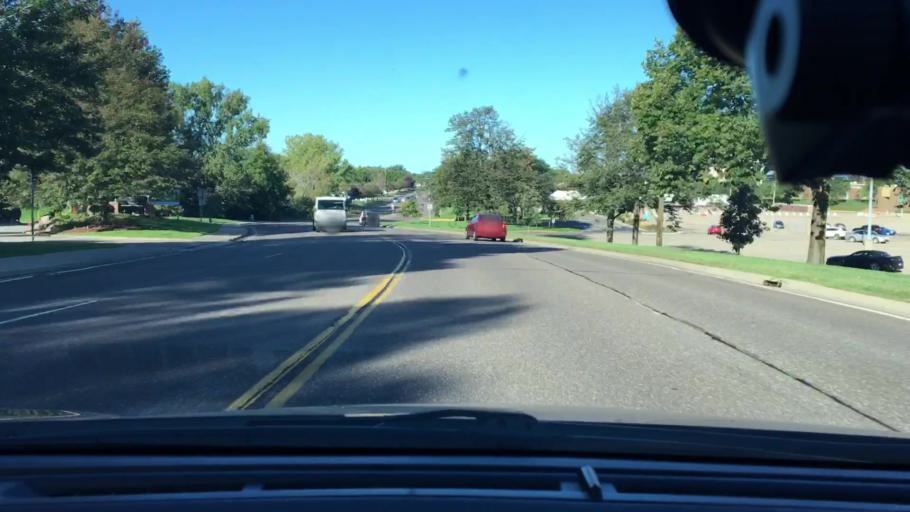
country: US
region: Minnesota
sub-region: Hennepin County
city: Minnetonka Mills
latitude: 44.9659
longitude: -93.4360
